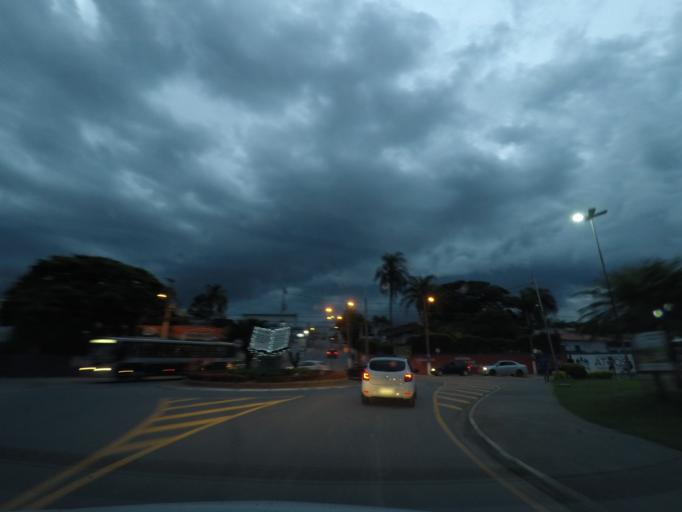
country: BR
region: Sao Paulo
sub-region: Vinhedo
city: Vinhedo
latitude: -23.0436
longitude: -47.0090
